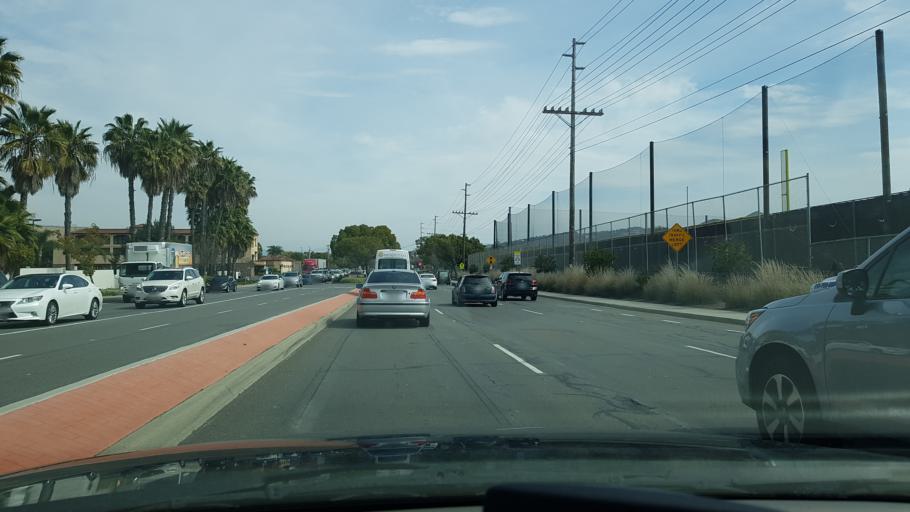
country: US
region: California
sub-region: San Diego County
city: Lake San Marcos
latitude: 33.1314
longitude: -117.2041
